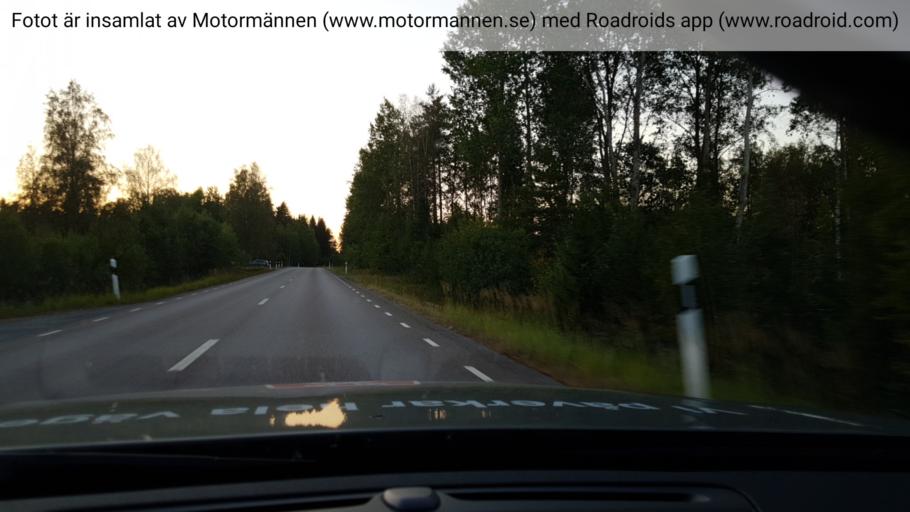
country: SE
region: Uppsala
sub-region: Heby Kommun
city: OEstervala
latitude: 60.0589
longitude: 17.2237
